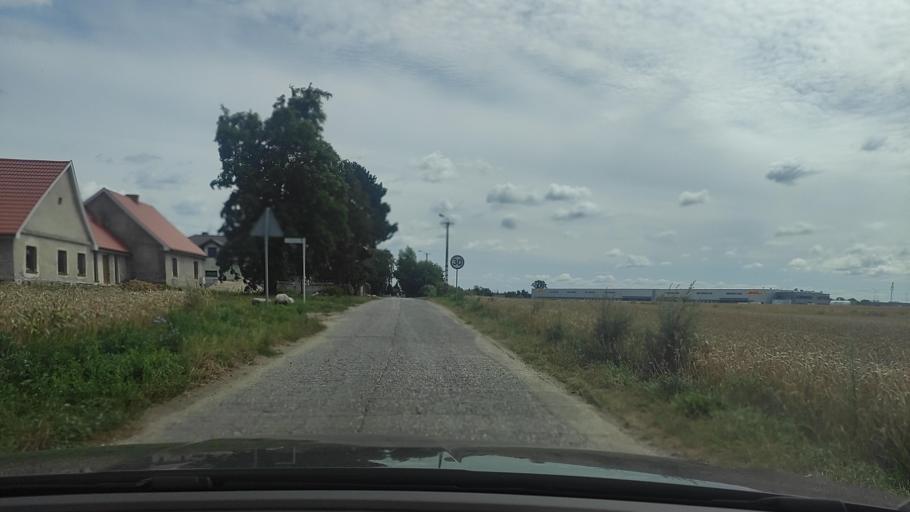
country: PL
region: Greater Poland Voivodeship
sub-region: Powiat poznanski
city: Kostrzyn
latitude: 52.4050
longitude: 17.2028
